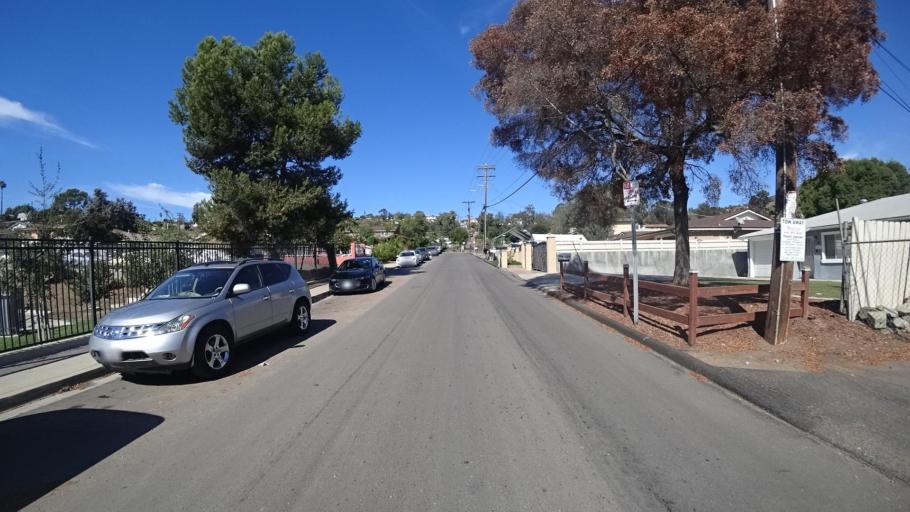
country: US
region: California
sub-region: San Diego County
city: La Presa
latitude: 32.7180
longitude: -117.0058
